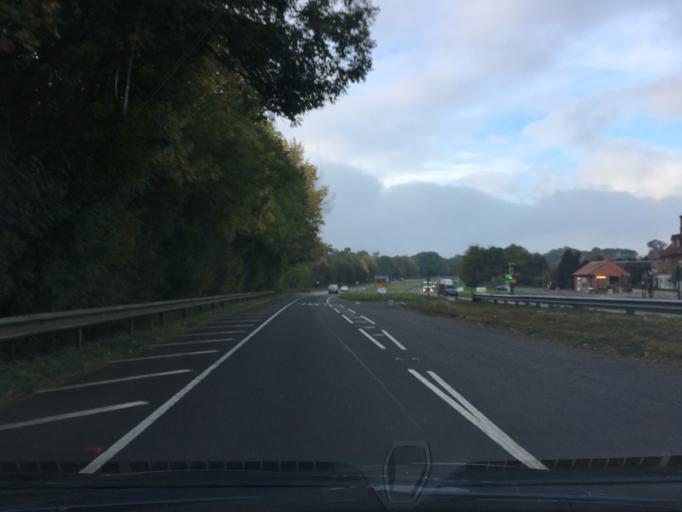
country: GB
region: England
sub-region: Hampshire
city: Long Sutton
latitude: 51.1750
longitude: -0.9181
